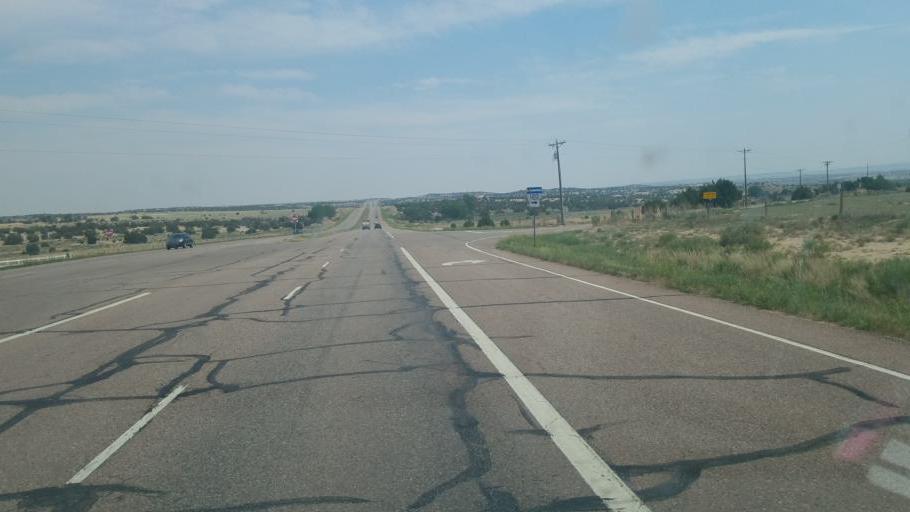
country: US
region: Colorado
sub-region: Fremont County
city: Penrose
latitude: 38.3919
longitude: -104.9690
